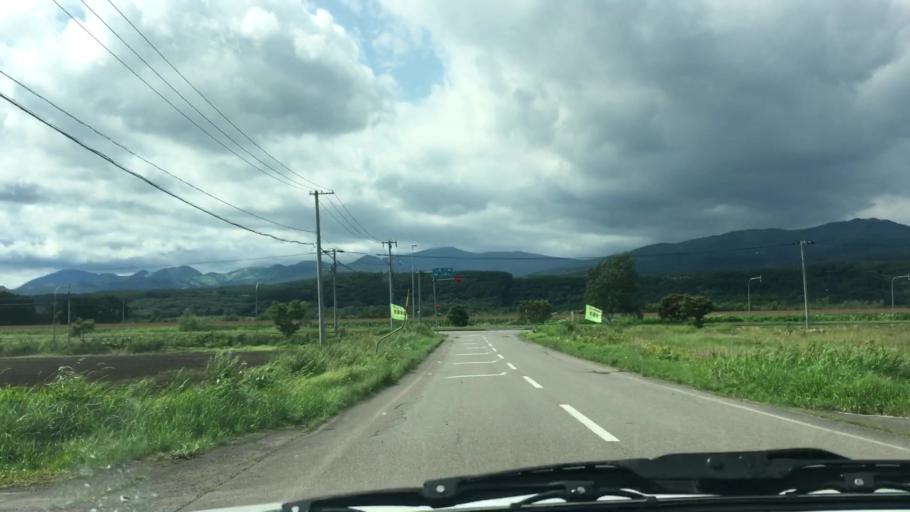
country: JP
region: Hokkaido
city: Otofuke
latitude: 43.2841
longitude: 143.3080
